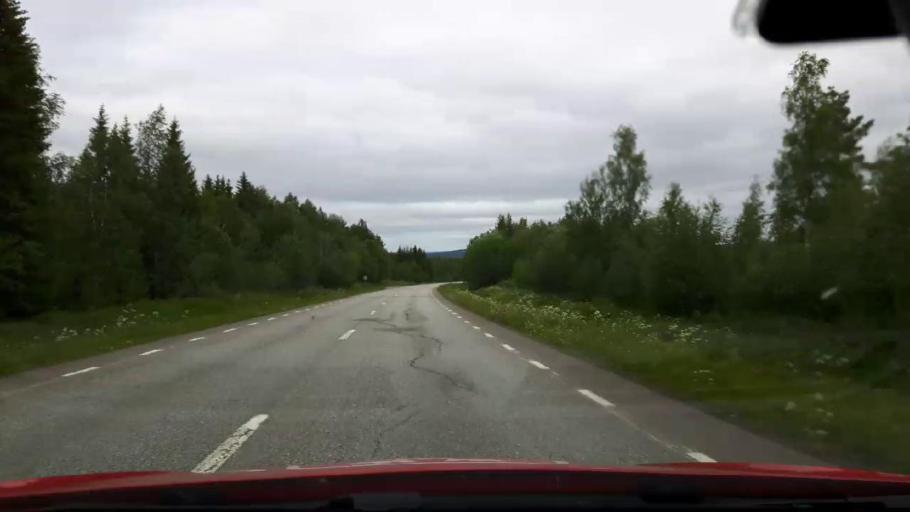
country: SE
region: Jaemtland
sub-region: Krokoms Kommun
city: Krokom
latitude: 63.5865
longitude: 14.6367
